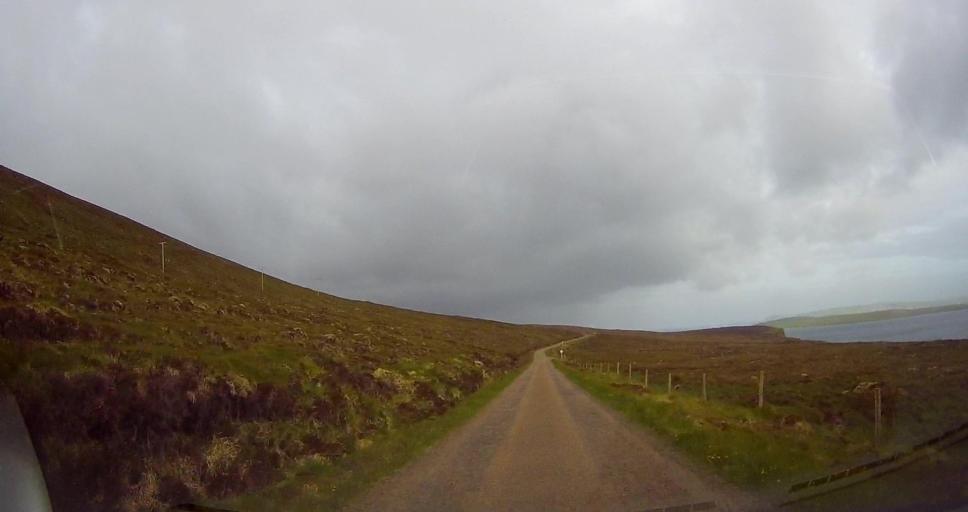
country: GB
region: Scotland
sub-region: Orkney Islands
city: Stromness
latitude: 58.8903
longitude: -3.2580
